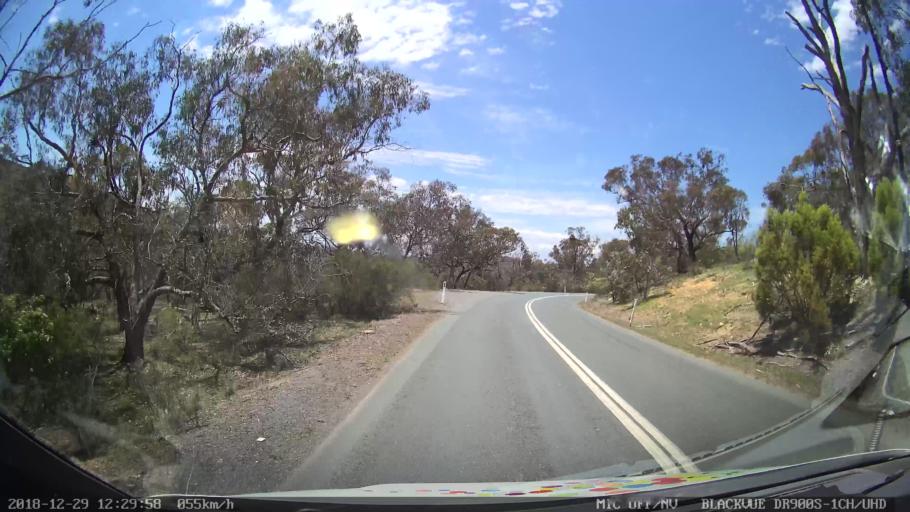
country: AU
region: Australian Capital Territory
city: Macarthur
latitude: -35.5023
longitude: 149.2323
